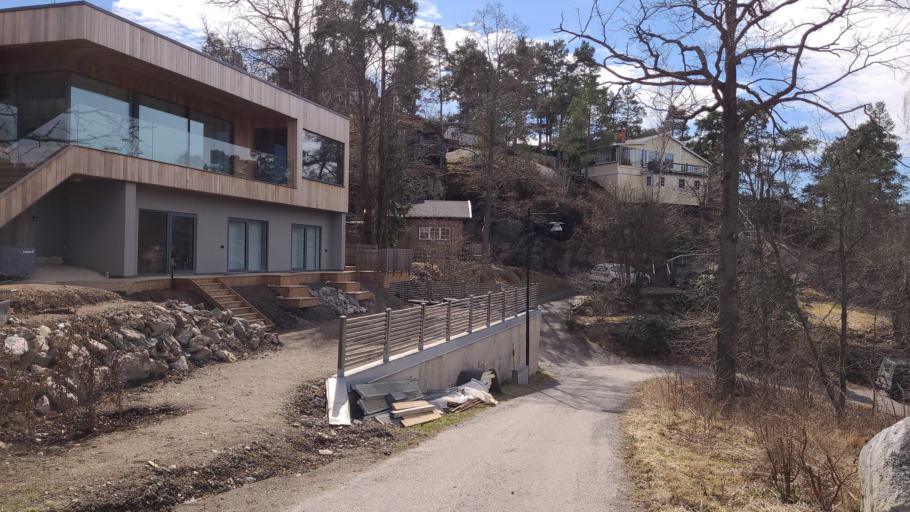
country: SE
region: Stockholm
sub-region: Lidingo
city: Brevik
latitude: 59.3301
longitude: 18.2201
